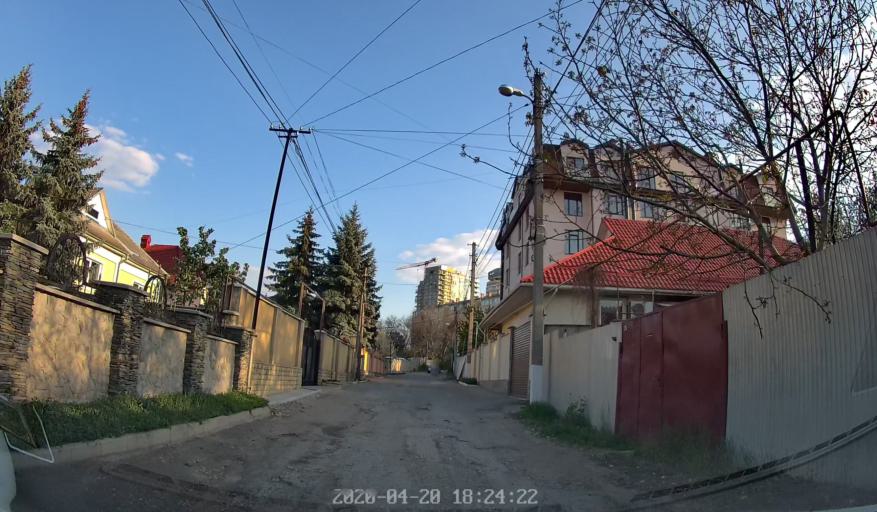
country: MD
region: Chisinau
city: Chisinau
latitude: 46.9943
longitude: 28.8378
